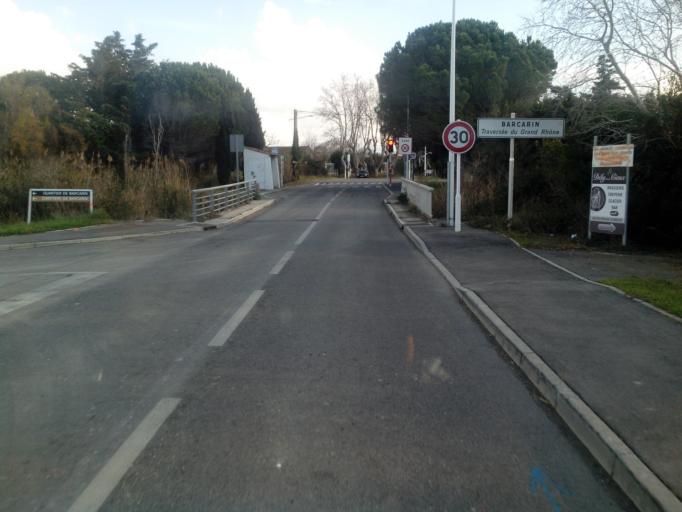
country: FR
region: Provence-Alpes-Cote d'Azur
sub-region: Departement des Bouches-du-Rhone
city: Port-Saint-Louis-du-Rhone
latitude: 43.4201
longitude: 4.7330
